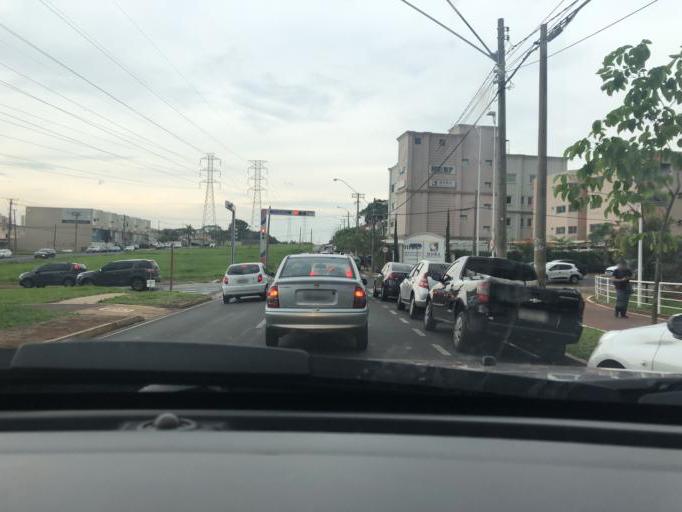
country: BR
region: Sao Paulo
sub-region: Sao Jose Do Rio Preto
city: Sao Jose do Rio Preto
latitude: -20.8445
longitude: -49.3941
